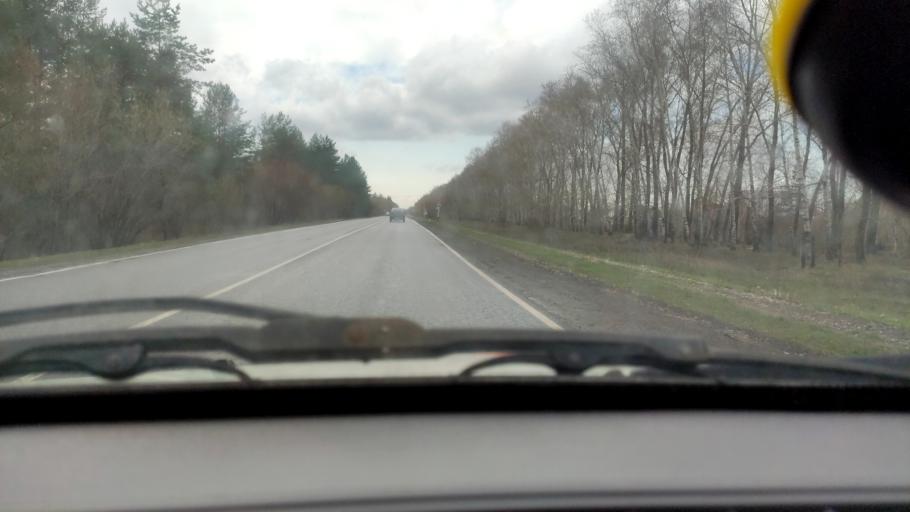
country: RU
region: Samara
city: Povolzhskiy
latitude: 53.6109
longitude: 49.6181
